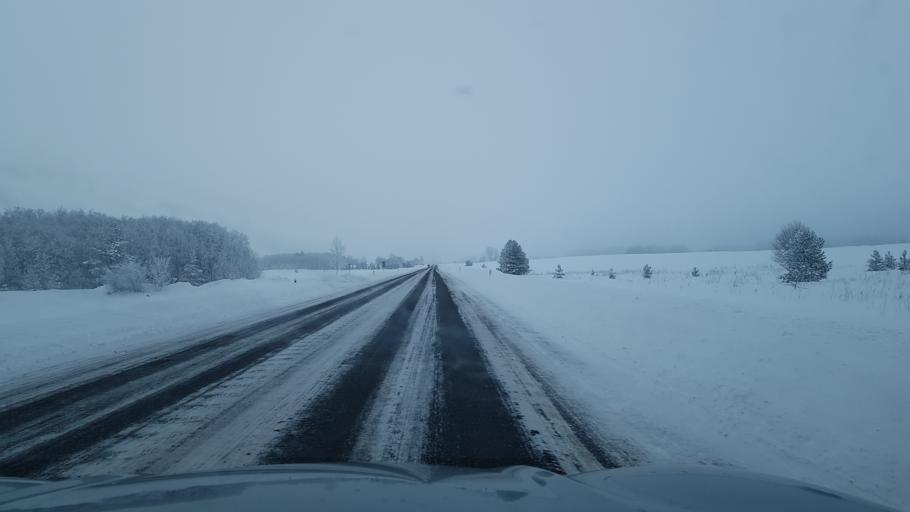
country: EE
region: Ida-Virumaa
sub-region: Johvi vald
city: Johvi
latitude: 59.2417
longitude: 27.3593
